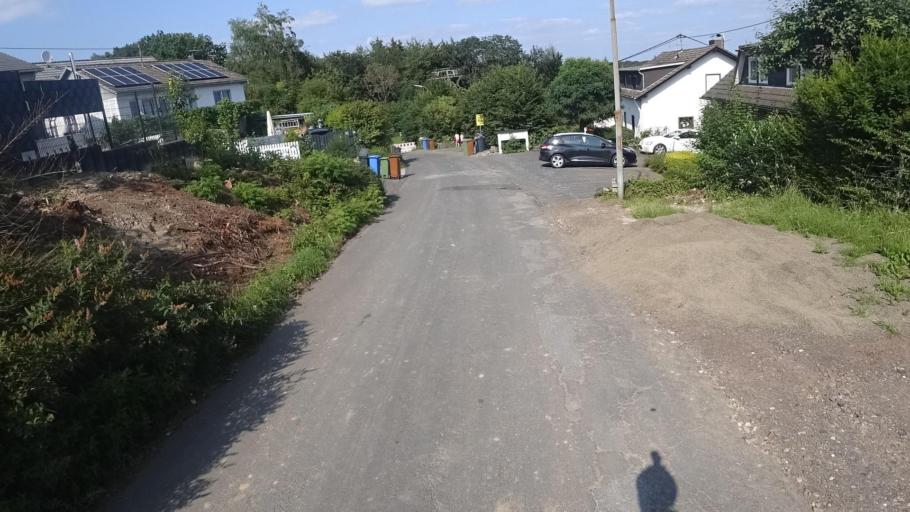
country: DE
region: Rheinland-Pfalz
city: Sankt Katharinen
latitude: 50.5594
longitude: 7.3563
